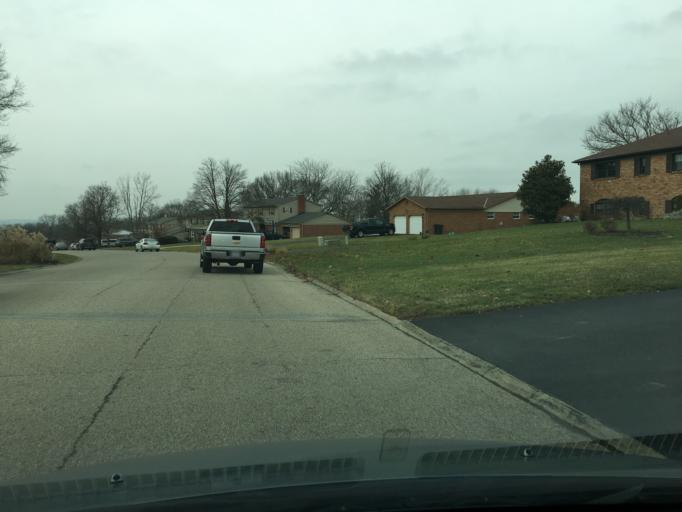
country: US
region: Ohio
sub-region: Hamilton County
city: Sharonville
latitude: 39.2995
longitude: -84.3931
